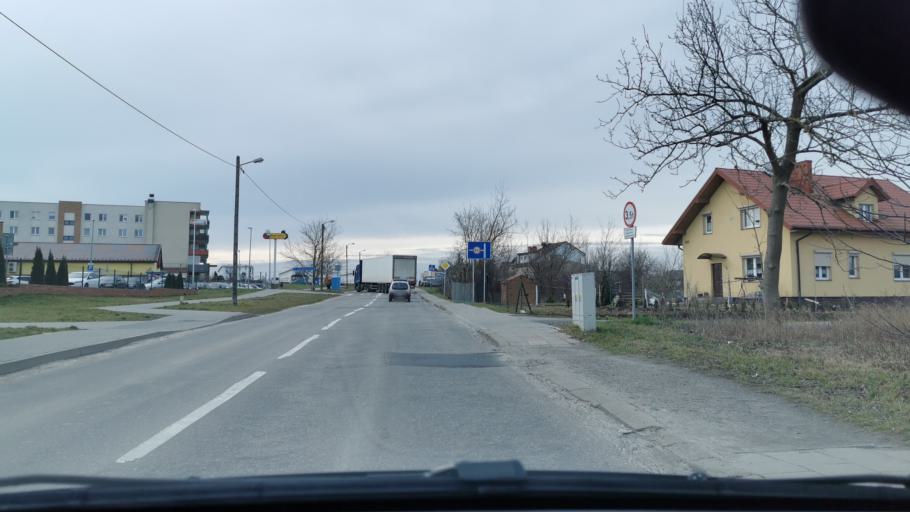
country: PL
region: Lublin Voivodeship
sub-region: Powiat lubelski
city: Lublin
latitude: 51.1996
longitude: 22.5419
